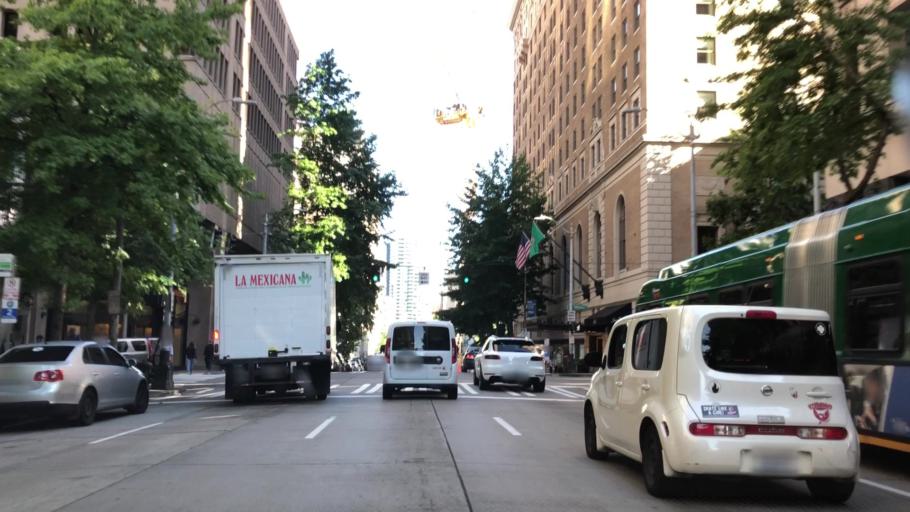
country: US
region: Washington
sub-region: King County
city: Seattle
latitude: 47.6072
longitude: -122.3340
